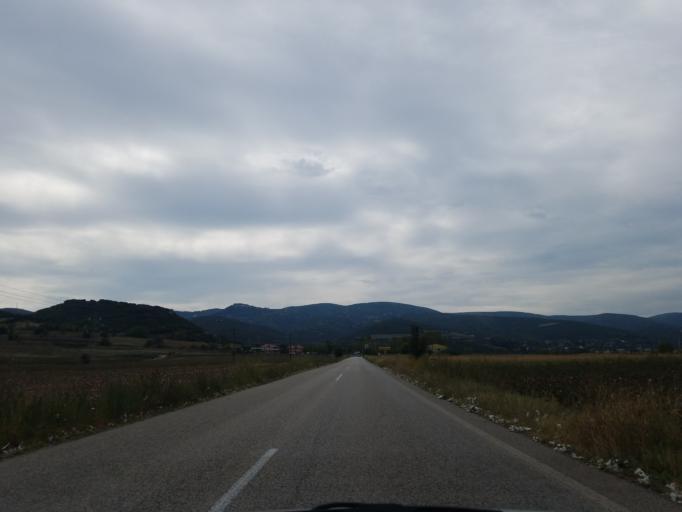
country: GR
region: Central Greece
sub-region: Nomos Fthiotidos
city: Domokos
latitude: 39.1616
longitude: 22.2937
